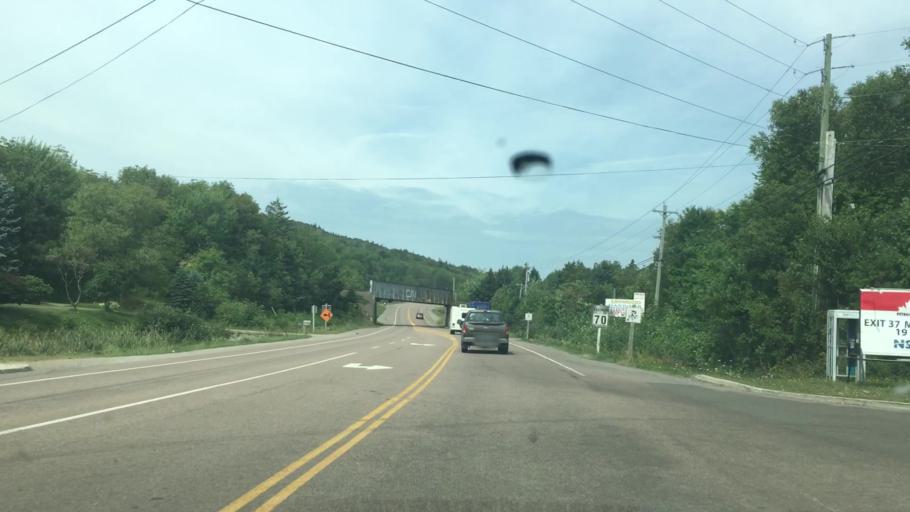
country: CA
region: Nova Scotia
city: Port Hawkesbury
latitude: 45.6532
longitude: -61.4450
